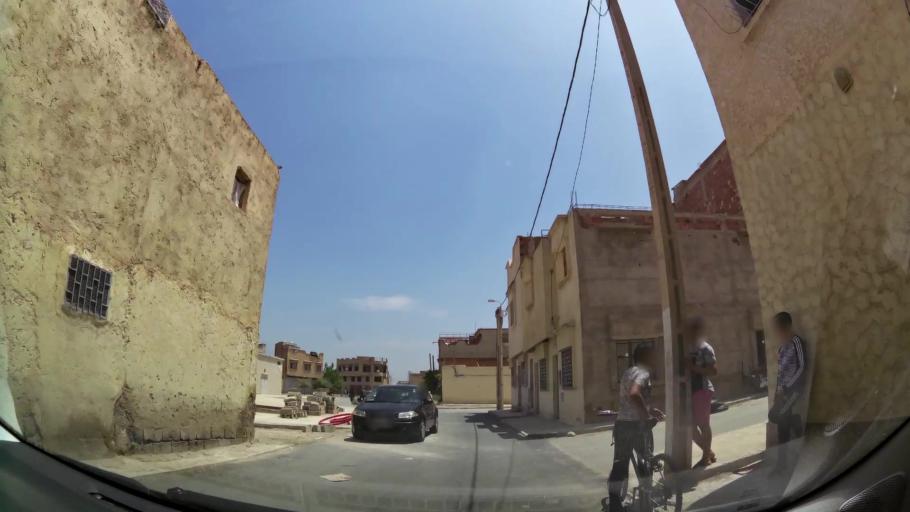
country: MA
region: Oriental
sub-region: Oujda-Angad
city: Oujda
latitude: 34.6827
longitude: -1.8999
